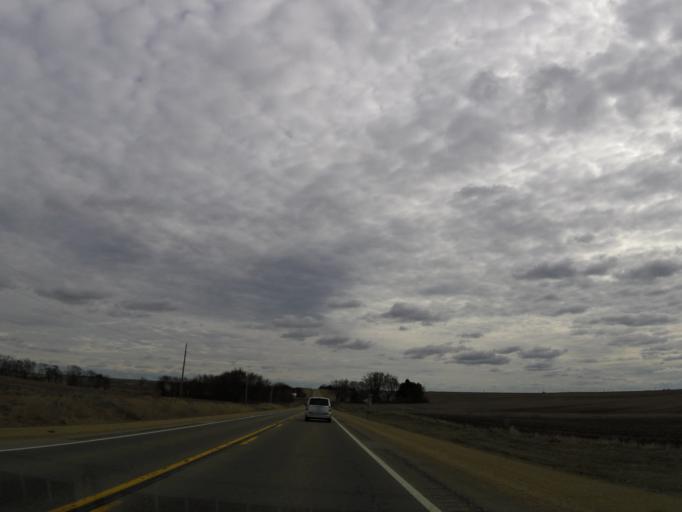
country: US
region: Iowa
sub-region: Chickasaw County
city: New Hampton
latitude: 43.1745
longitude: -92.2987
